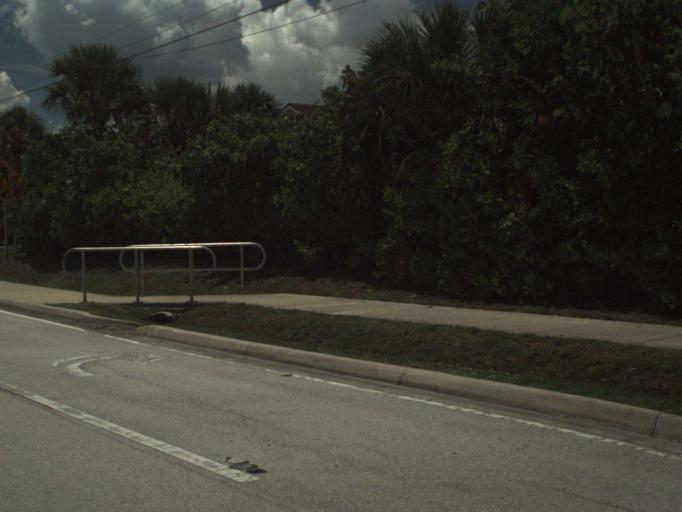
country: US
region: Florida
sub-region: Martin County
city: Sewall's Point
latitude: 27.2306
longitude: -80.1843
